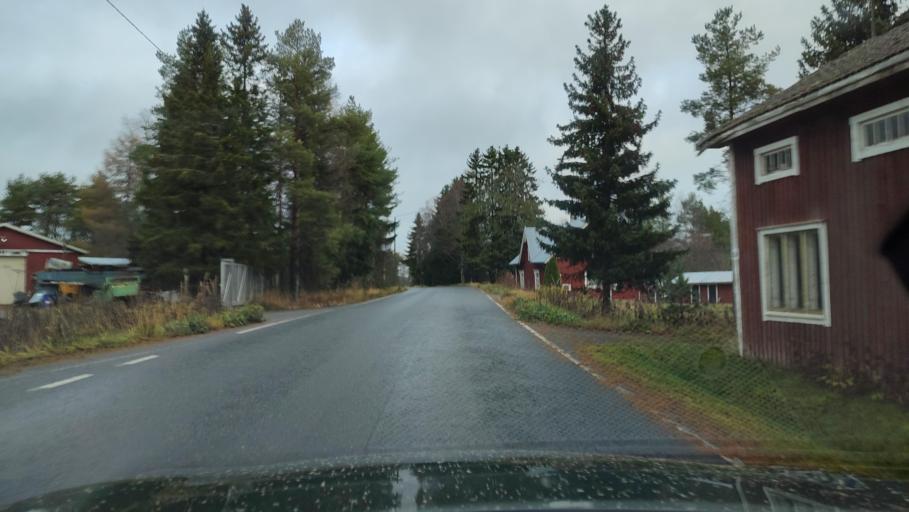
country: FI
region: Southern Ostrobothnia
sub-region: Suupohja
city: Karijoki
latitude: 62.3788
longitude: 21.5547
